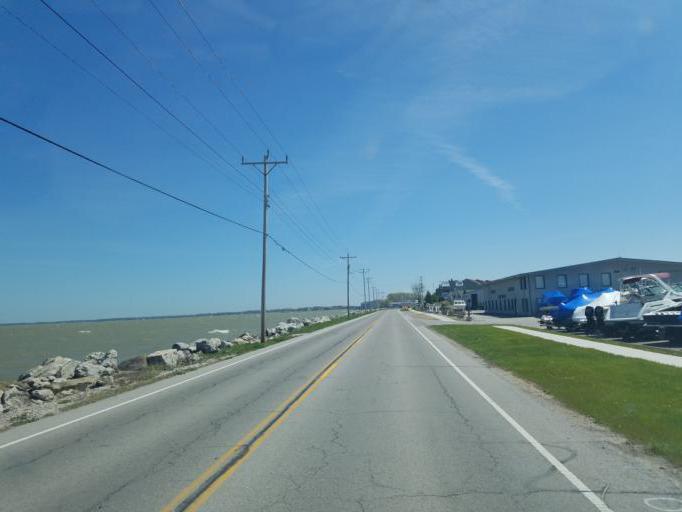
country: US
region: Ohio
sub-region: Ottawa County
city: Port Clinton
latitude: 41.5195
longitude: -82.9532
